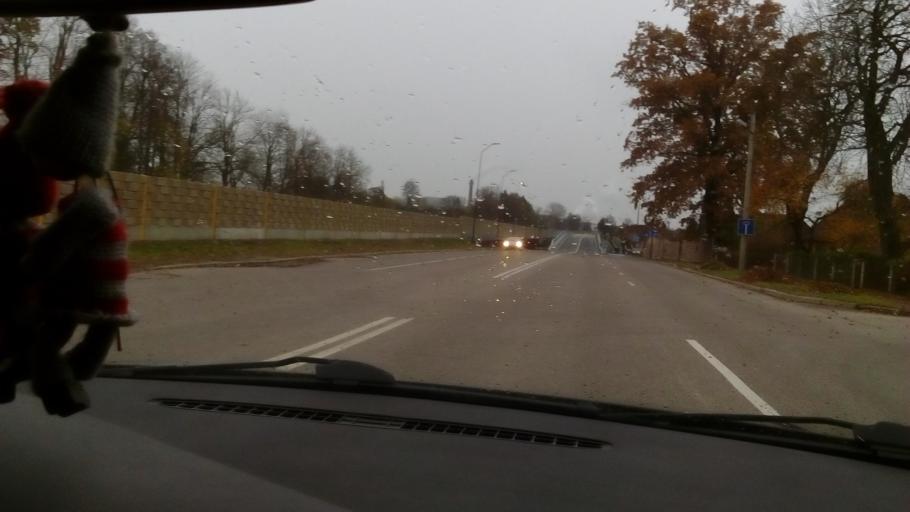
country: LT
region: Marijampoles apskritis
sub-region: Marijampole Municipality
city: Marijampole
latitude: 54.5464
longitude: 23.3570
